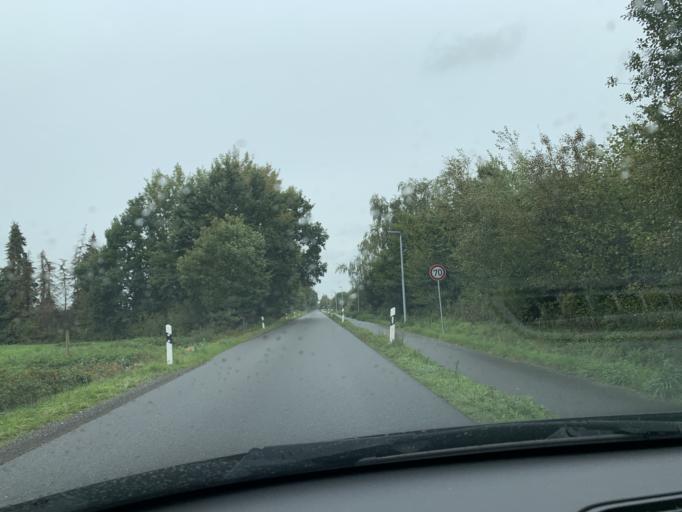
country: DE
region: Lower Saxony
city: Edewecht
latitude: 53.1264
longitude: 8.0831
